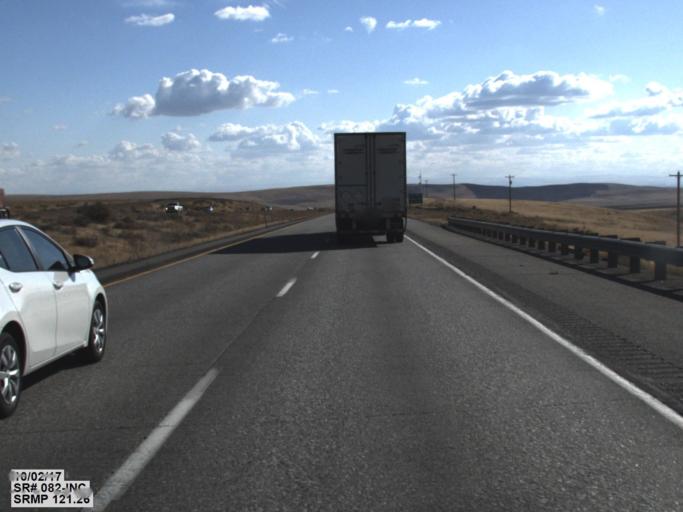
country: US
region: Washington
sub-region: Benton County
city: Highland
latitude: 46.0469
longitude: -119.2245
